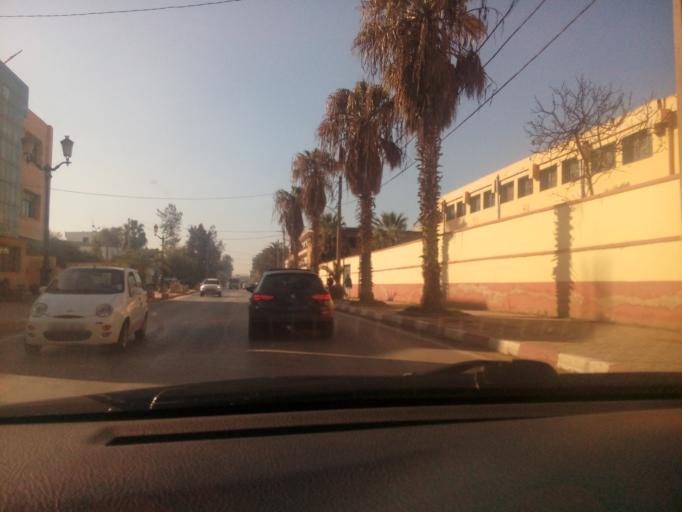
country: DZ
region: Oran
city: Es Senia
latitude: 35.6484
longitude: -0.6184
